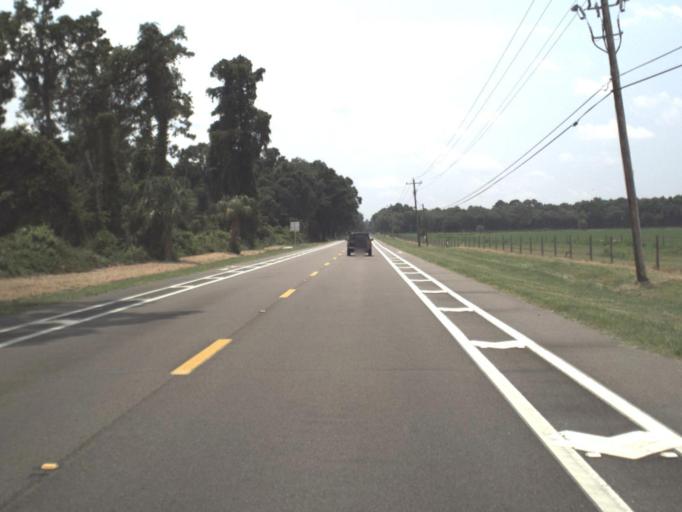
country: US
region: Florida
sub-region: Levy County
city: Manatee Road
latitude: 29.4963
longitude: -82.9478
